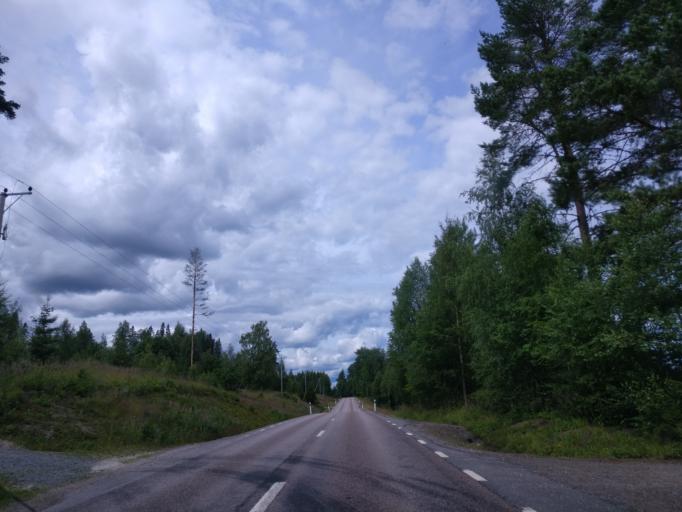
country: SE
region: Vaermland
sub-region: Hagfors Kommun
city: Ekshaerad
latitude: 60.1843
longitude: 13.3430
